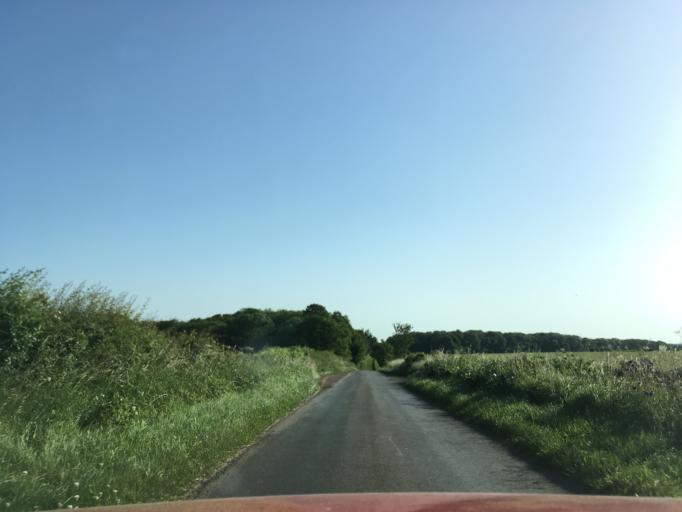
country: GB
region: England
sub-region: Gloucestershire
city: Lechlade
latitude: 51.7696
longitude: -1.7115
